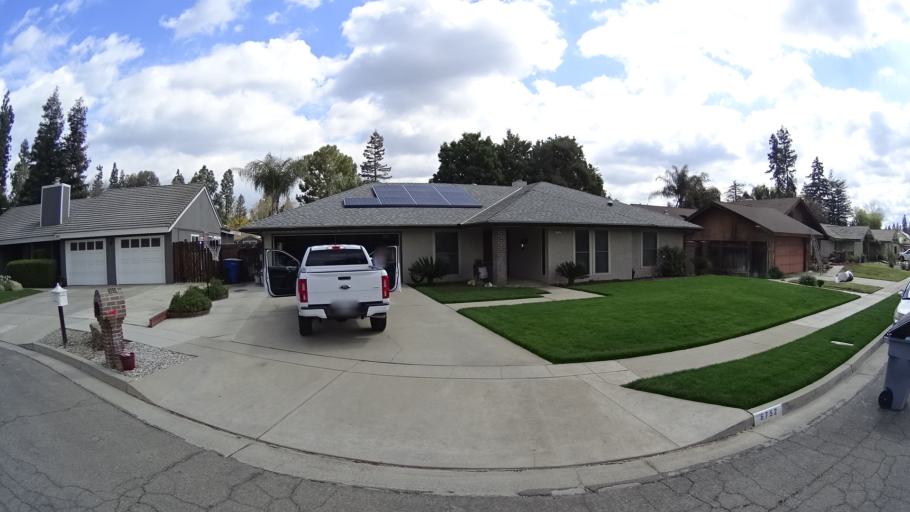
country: US
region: California
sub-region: Fresno County
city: Fresno
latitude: 36.8363
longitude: -119.8576
